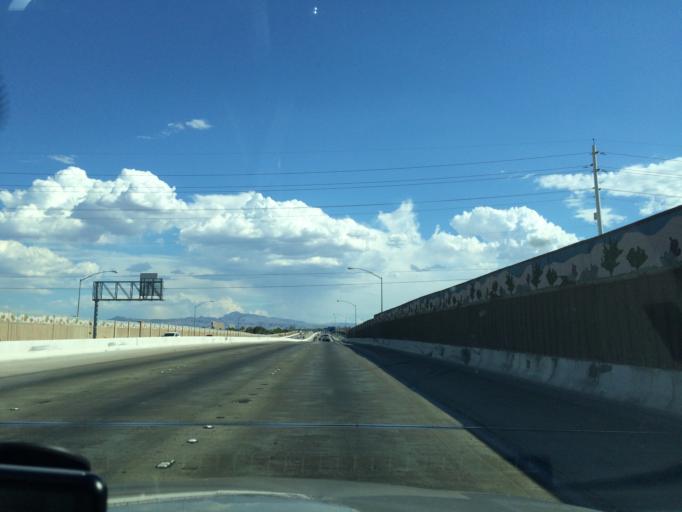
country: US
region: Nevada
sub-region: Clark County
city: Winchester
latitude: 36.1595
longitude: -115.0918
